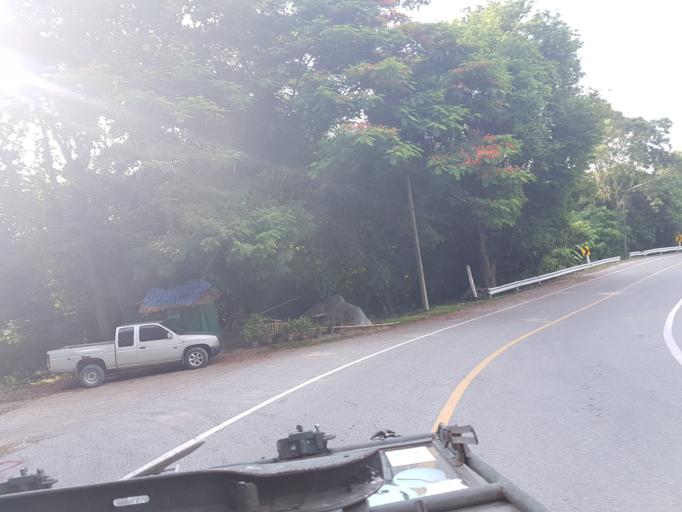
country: TH
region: Pattani
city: Khok Pho
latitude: 6.6590
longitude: 101.0945
